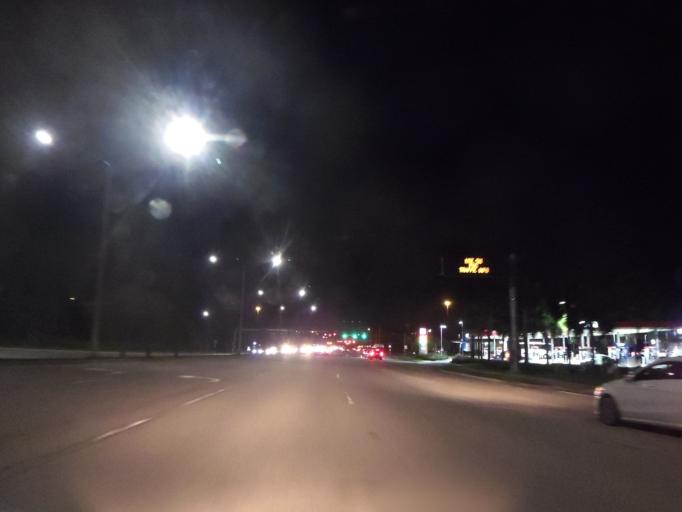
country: US
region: Florida
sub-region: Duval County
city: Jacksonville Beach
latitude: 30.2672
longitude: -81.5250
